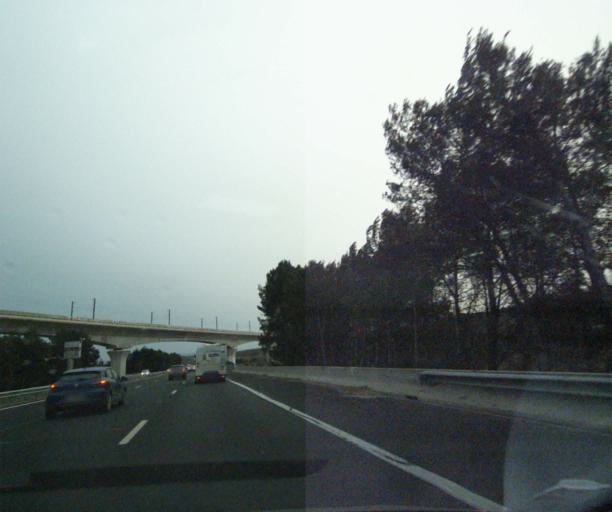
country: FR
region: Provence-Alpes-Cote d'Azur
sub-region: Departement des Bouches-du-Rhone
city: Ventabren
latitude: 43.5463
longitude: 5.3286
